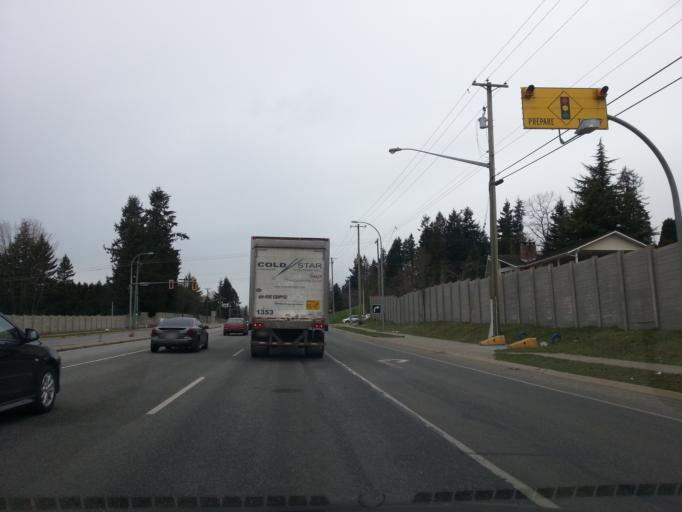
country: CA
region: British Columbia
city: Surrey
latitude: 49.1046
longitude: -122.8221
